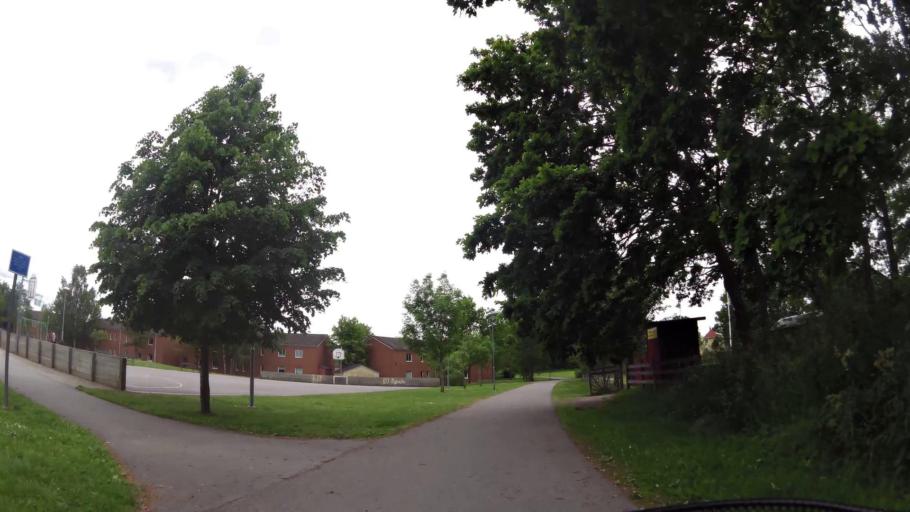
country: SE
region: OEstergoetland
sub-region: Linkopings Kommun
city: Malmslatt
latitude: 58.3856
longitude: 15.5633
